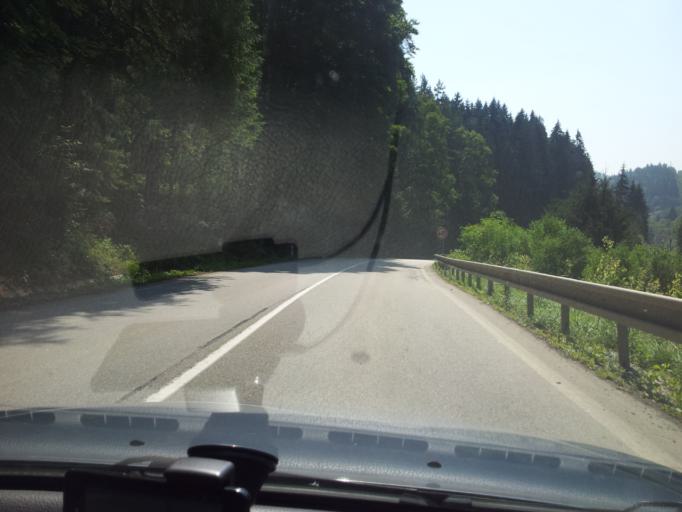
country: SK
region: Zilinsky
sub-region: Okres Dolny Kubin
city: Dolny Kubin
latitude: 49.2745
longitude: 19.3499
